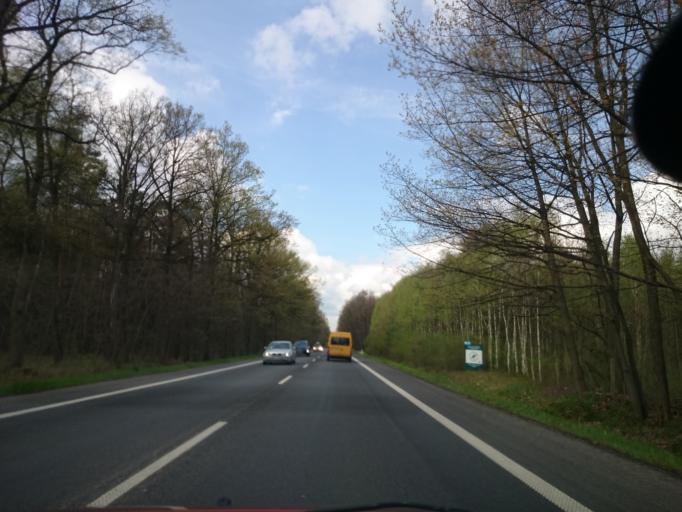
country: PL
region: Opole Voivodeship
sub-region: Powiat opolski
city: Naklo
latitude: 50.5894
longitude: 18.1002
